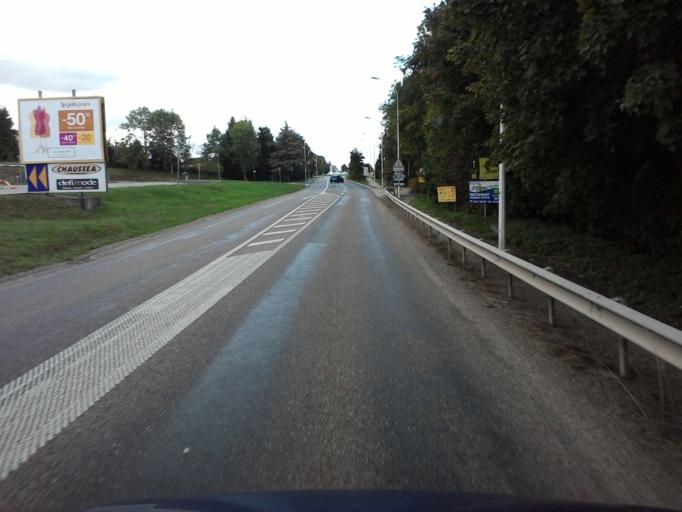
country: FR
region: Lorraine
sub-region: Departement des Vosges
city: Neufchateau
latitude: 48.3715
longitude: 5.7094
